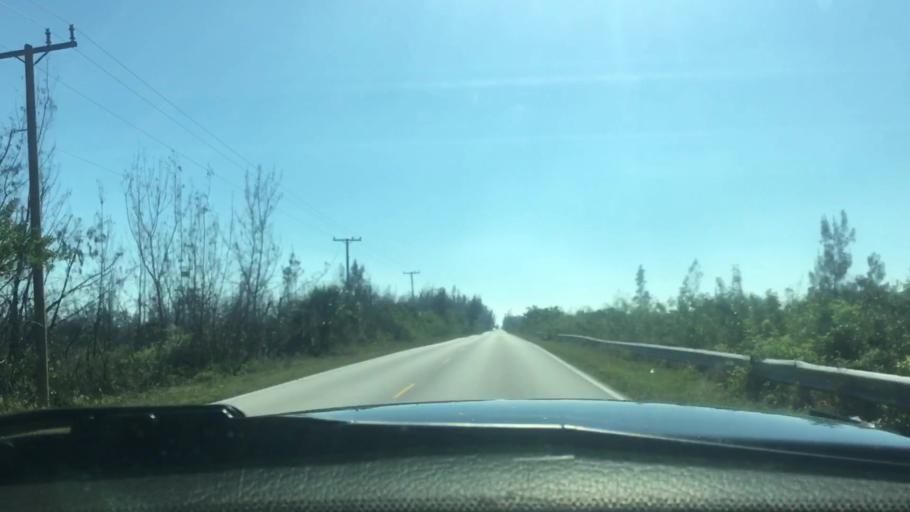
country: US
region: Florida
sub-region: Miami-Dade County
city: Florida City
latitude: 25.4248
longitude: -80.4676
